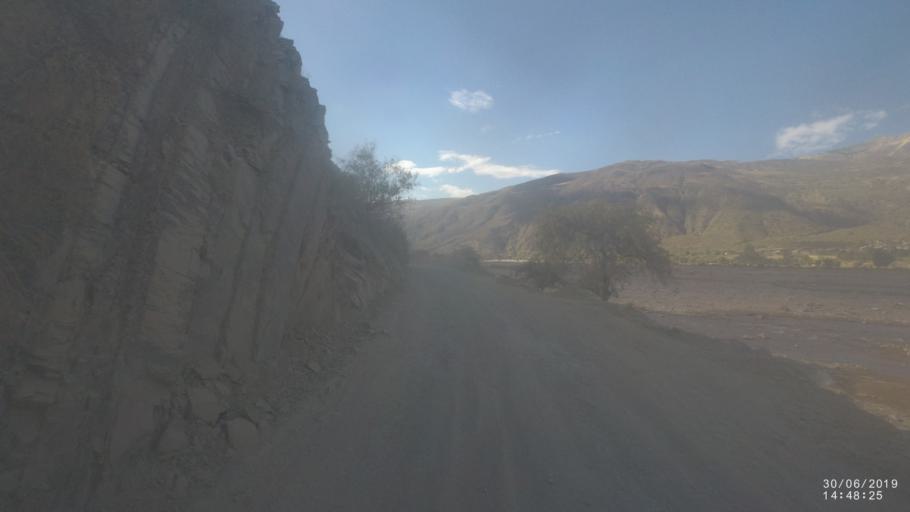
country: BO
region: Cochabamba
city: Irpa Irpa
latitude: -17.7893
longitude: -66.3429
